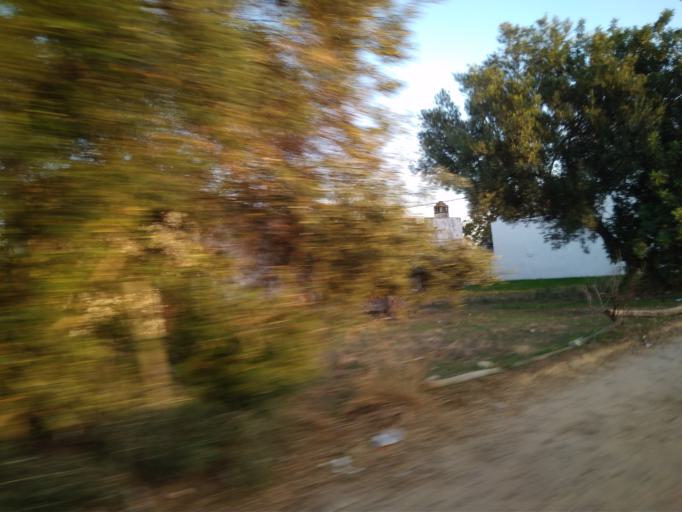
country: PT
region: Faro
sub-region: Faro
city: Santa Barbara de Nexe
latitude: 37.0753
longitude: -7.9597
